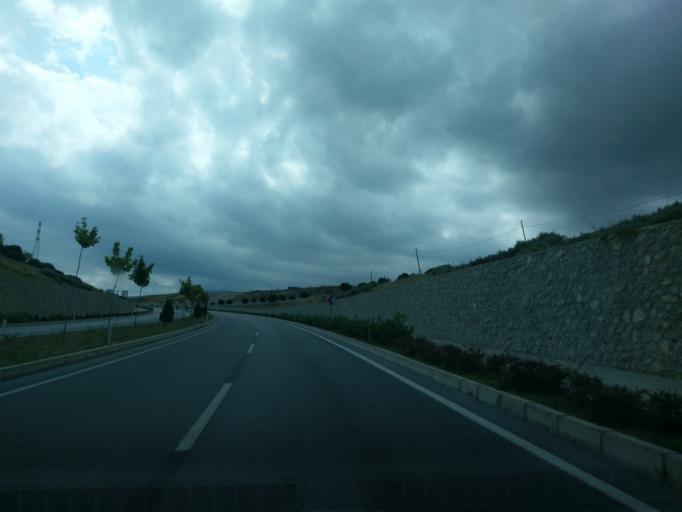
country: TR
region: Sinop
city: Gerze
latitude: 41.8116
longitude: 35.1673
